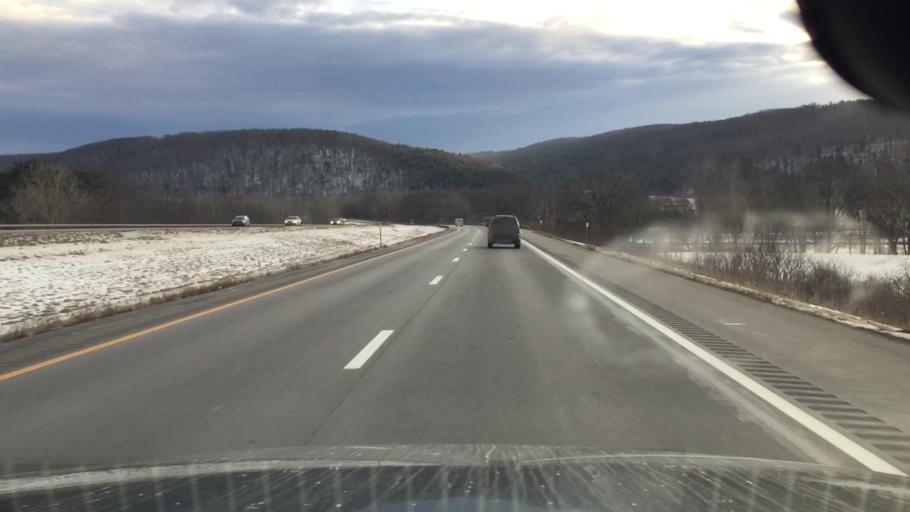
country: US
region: Pennsylvania
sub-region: Bradford County
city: Sayre
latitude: 42.0066
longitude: -76.4730
